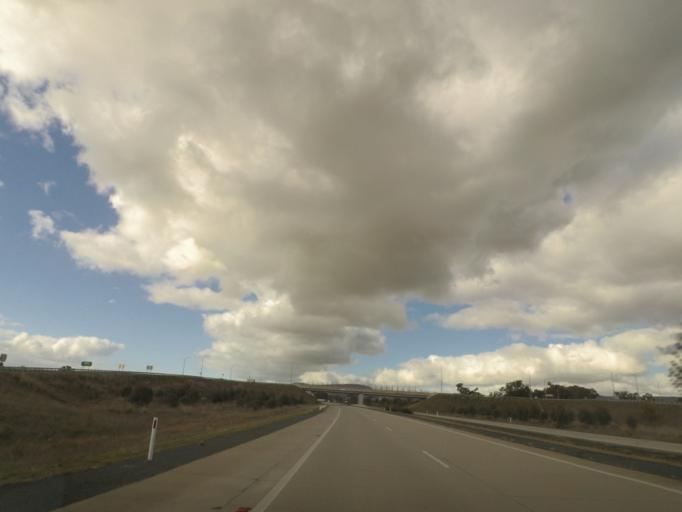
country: AU
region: New South Wales
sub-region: Greater Hume Shire
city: Holbrook
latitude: -35.7046
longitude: 147.3204
